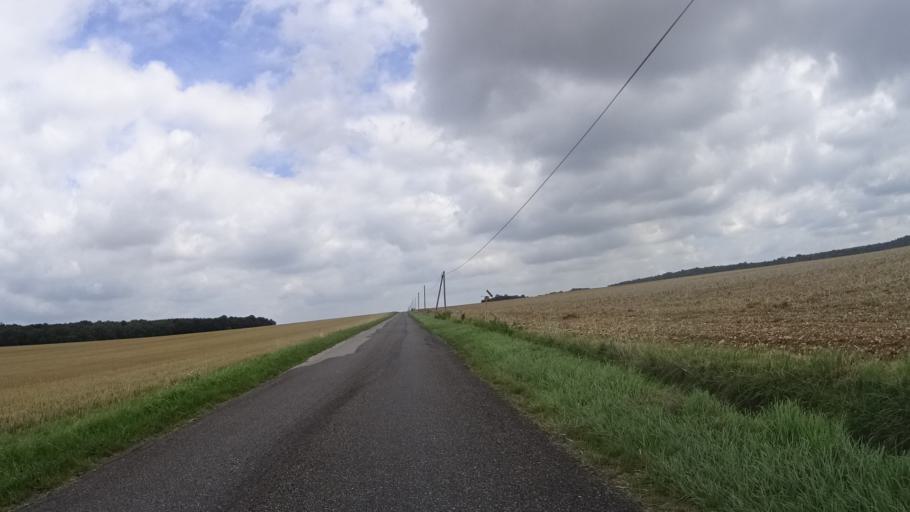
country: FR
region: Lorraine
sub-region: Departement de la Meuse
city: Ligny-en-Barrois
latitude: 48.7560
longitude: 5.4121
